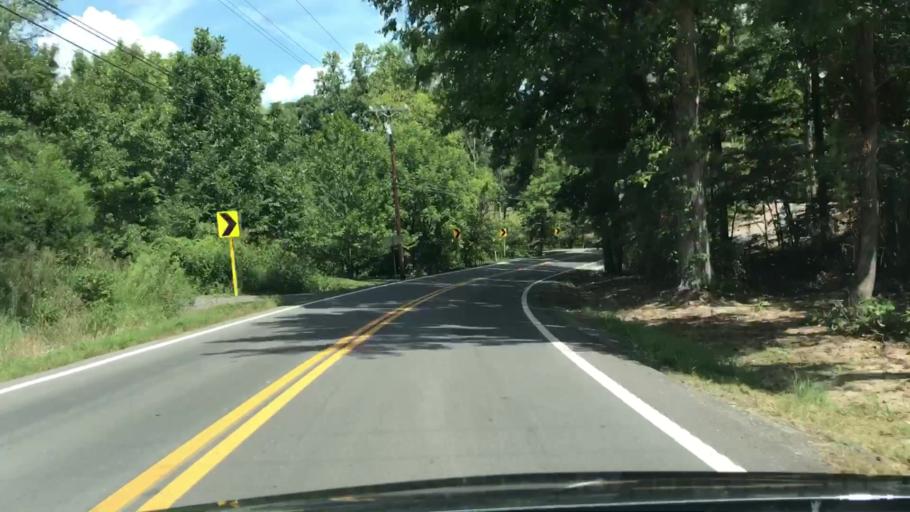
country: US
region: Tennessee
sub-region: Sumner County
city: Portland
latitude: 36.5188
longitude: -86.5611
